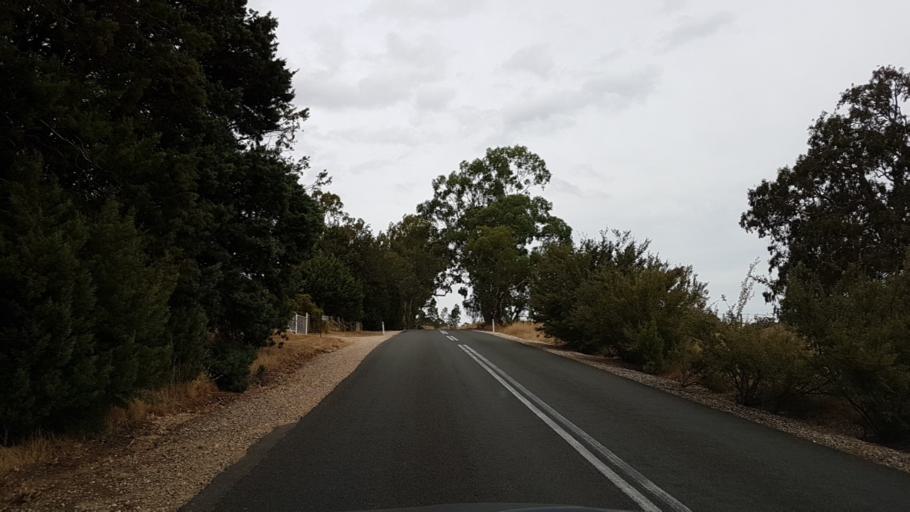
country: AU
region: South Australia
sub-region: Adelaide Hills
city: Gumeracha
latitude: -34.7712
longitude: 138.8889
